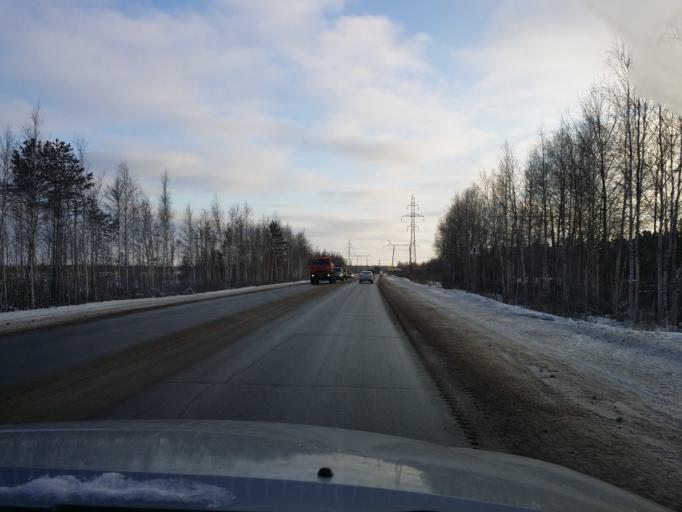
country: RU
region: Khanty-Mansiyskiy Avtonomnyy Okrug
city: Nizhnevartovsk
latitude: 61.0400
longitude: 76.3541
